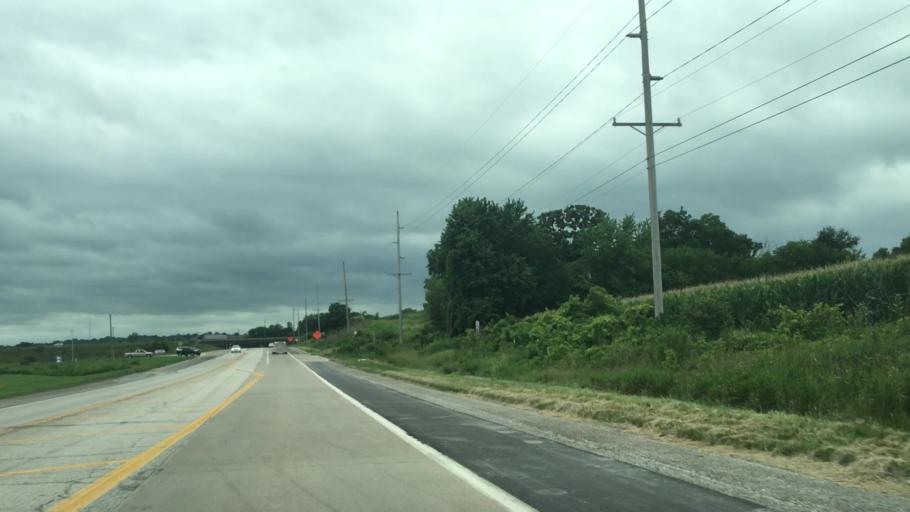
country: US
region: Iowa
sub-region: Johnson County
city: Tiffin
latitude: 41.7036
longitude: -91.6360
